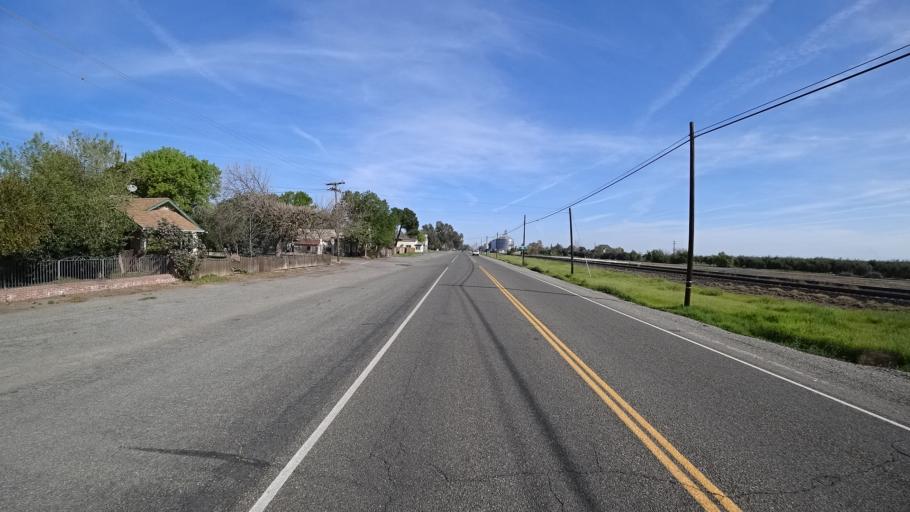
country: US
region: California
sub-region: Glenn County
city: Willows
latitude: 39.6171
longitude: -122.1941
